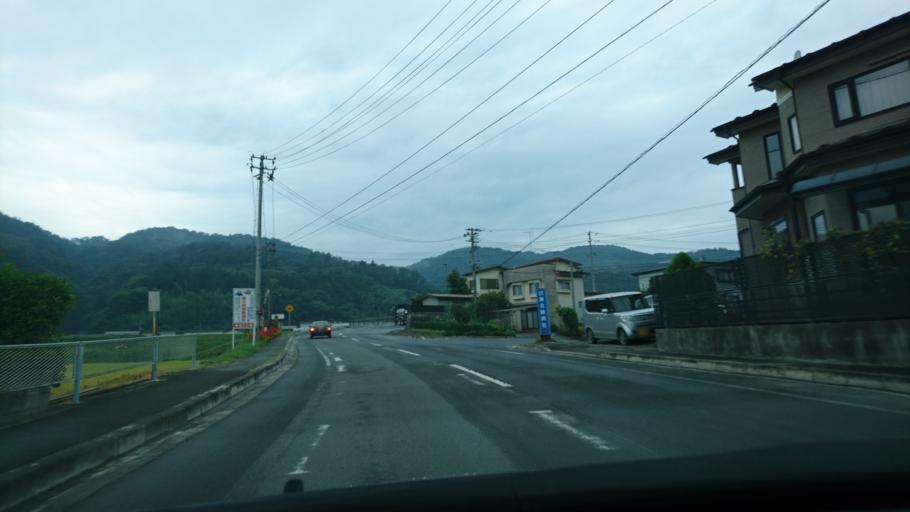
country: JP
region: Iwate
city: Ichinoseki
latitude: 38.9760
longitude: 141.2419
